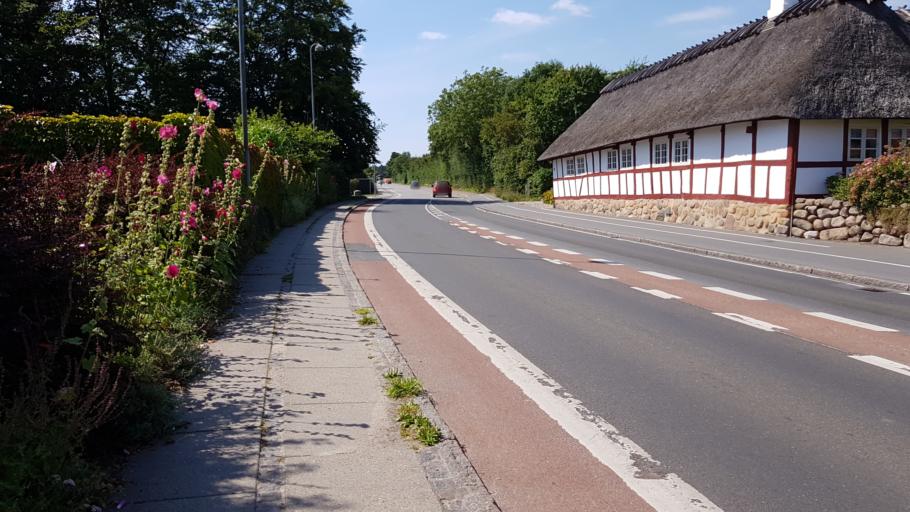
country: DK
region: South Denmark
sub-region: Svendborg Kommune
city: Svendborg
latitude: 55.0477
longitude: 10.5825
